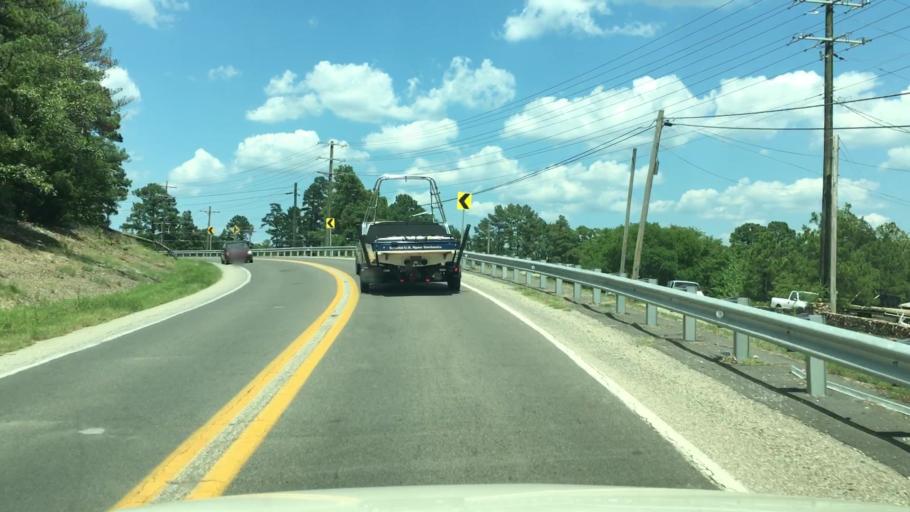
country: US
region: Arkansas
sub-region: Garland County
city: Lake Hamilton
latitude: 34.4045
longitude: -93.0913
